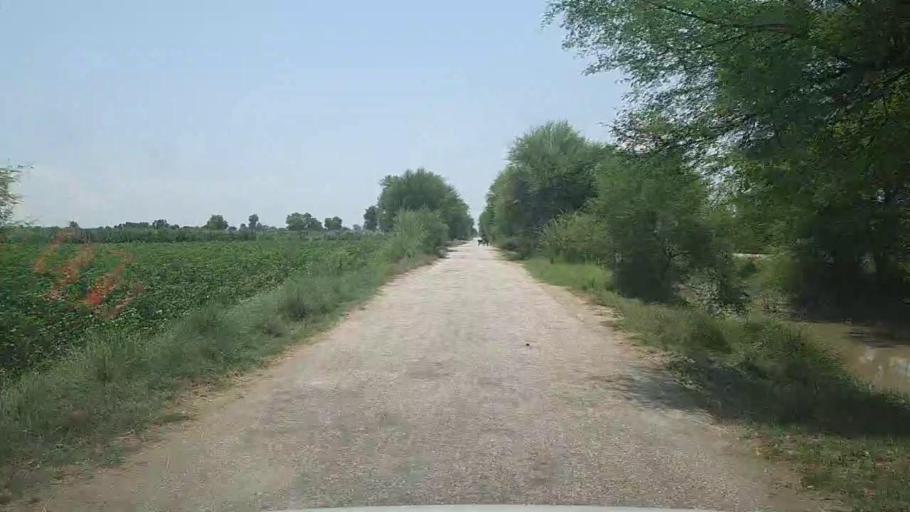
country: PK
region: Sindh
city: Ubauro
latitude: 28.1654
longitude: 69.7469
